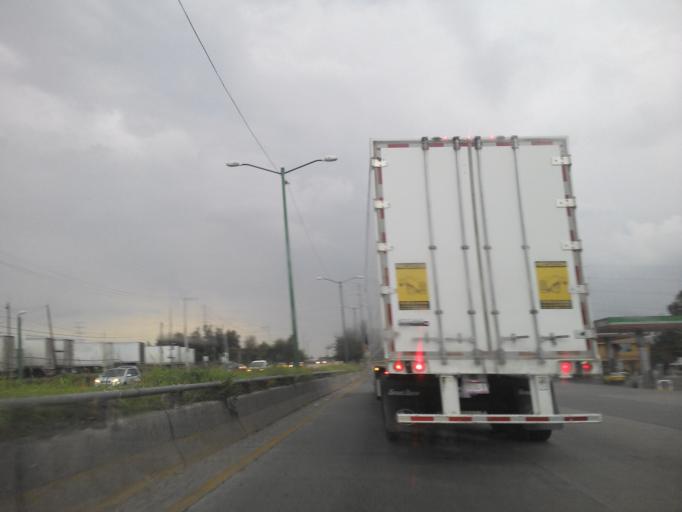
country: MX
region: Jalisco
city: Tlaquepaque
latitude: 20.6258
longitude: -103.2917
